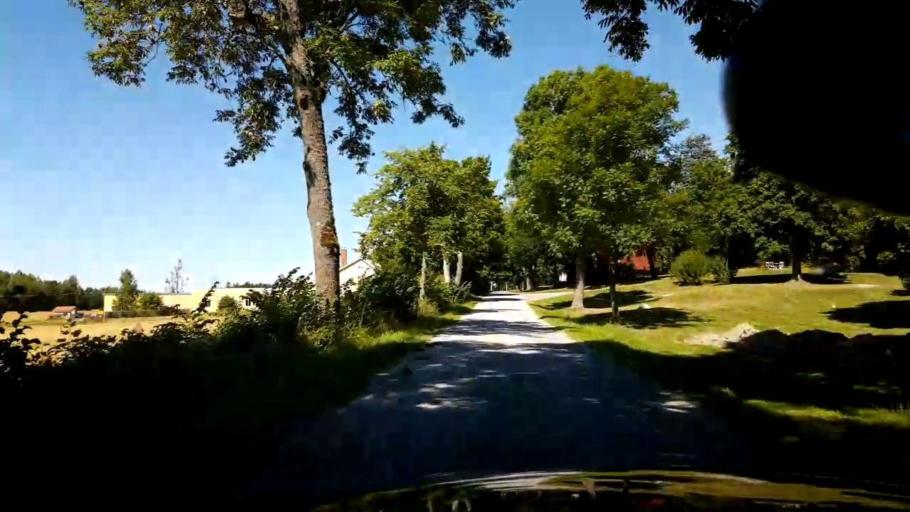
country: SE
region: Stockholm
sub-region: Sigtuna Kommun
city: Sigtuna
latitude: 59.6073
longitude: 17.6427
